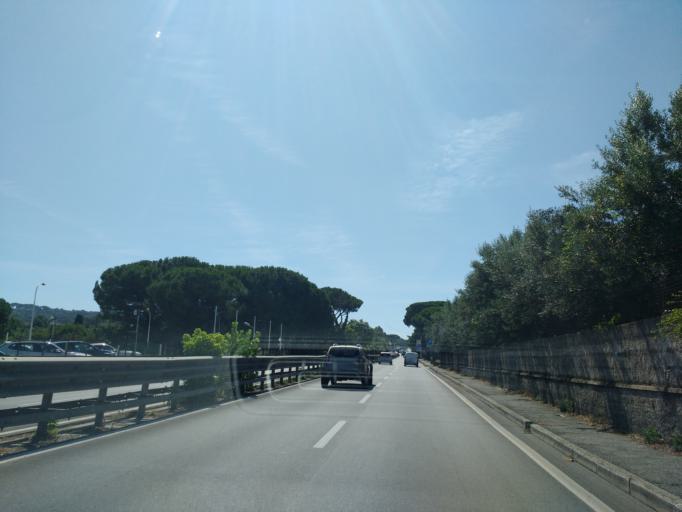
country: IT
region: Latium
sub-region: Citta metropolitana di Roma Capitale
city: Marino
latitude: 41.7588
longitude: 12.6251
